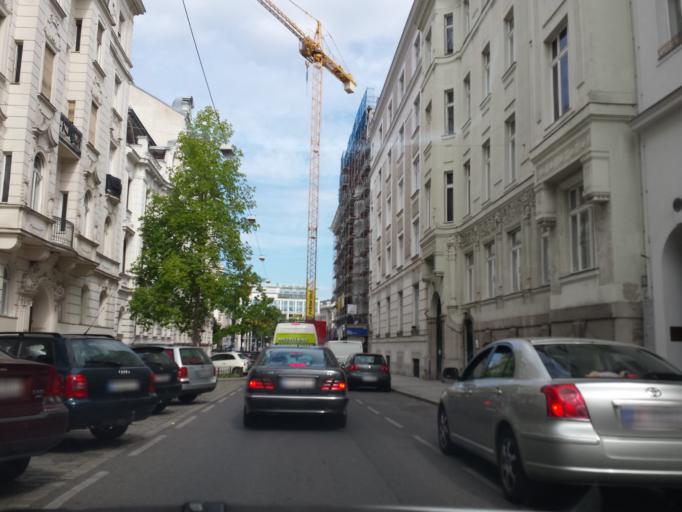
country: AT
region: Vienna
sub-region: Wien Stadt
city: Vienna
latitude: 48.1979
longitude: 16.3732
